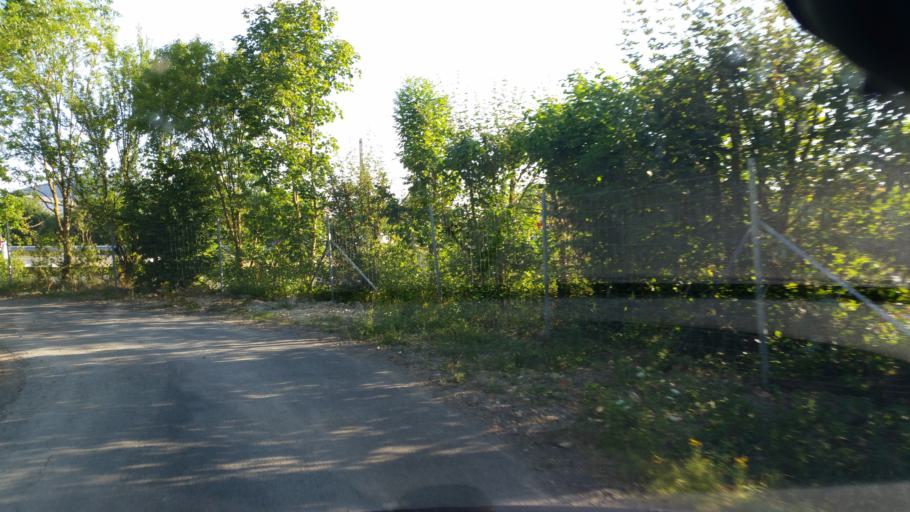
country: FR
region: Poitou-Charentes
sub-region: Departement de la Charente-Maritime
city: Saint-Jean-de-Liversay
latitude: 46.2264
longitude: -0.8802
